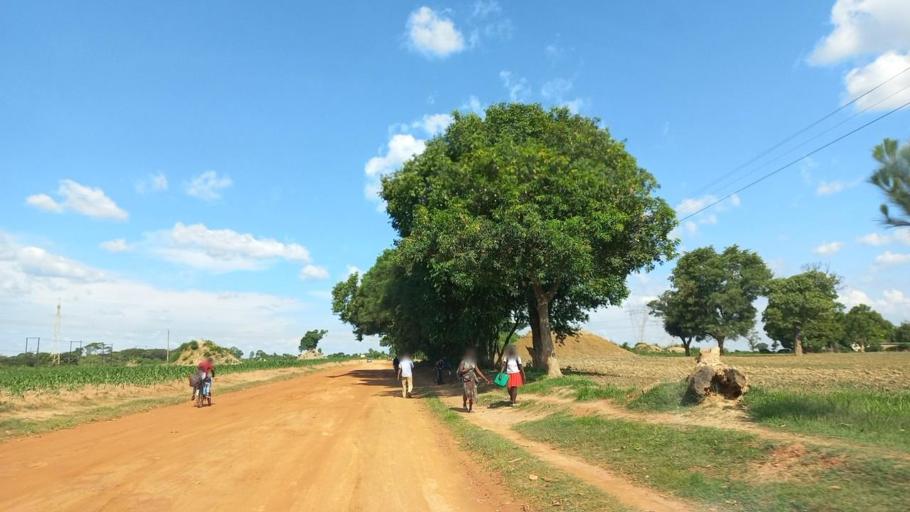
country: ZM
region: Copperbelt
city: Kitwe
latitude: -12.8714
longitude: 28.3418
